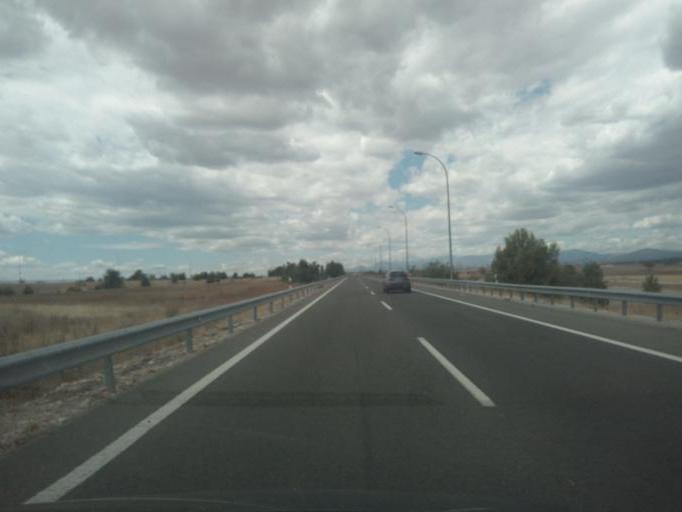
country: ES
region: Madrid
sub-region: Provincia de Madrid
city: San Sebastian de los Reyes
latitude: 40.5450
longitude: -3.5689
